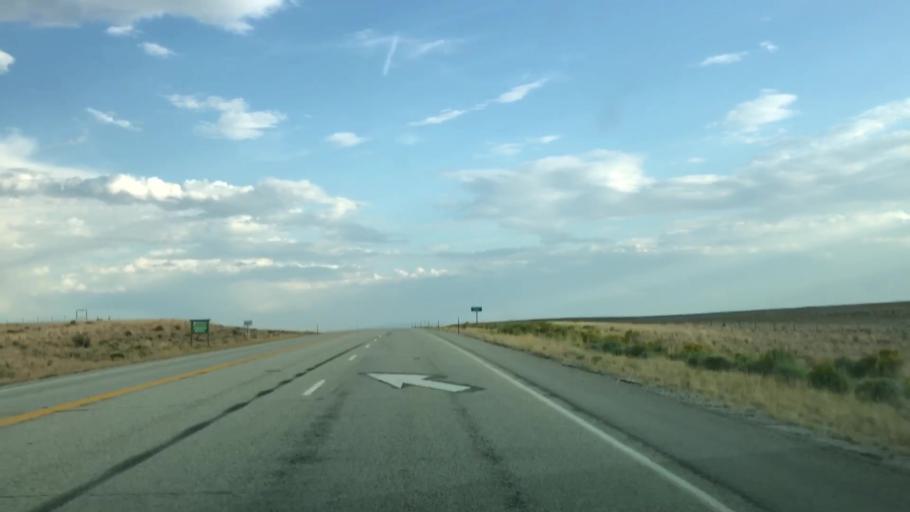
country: US
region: Wyoming
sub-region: Sweetwater County
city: North Rock Springs
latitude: 42.2643
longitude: -109.4746
